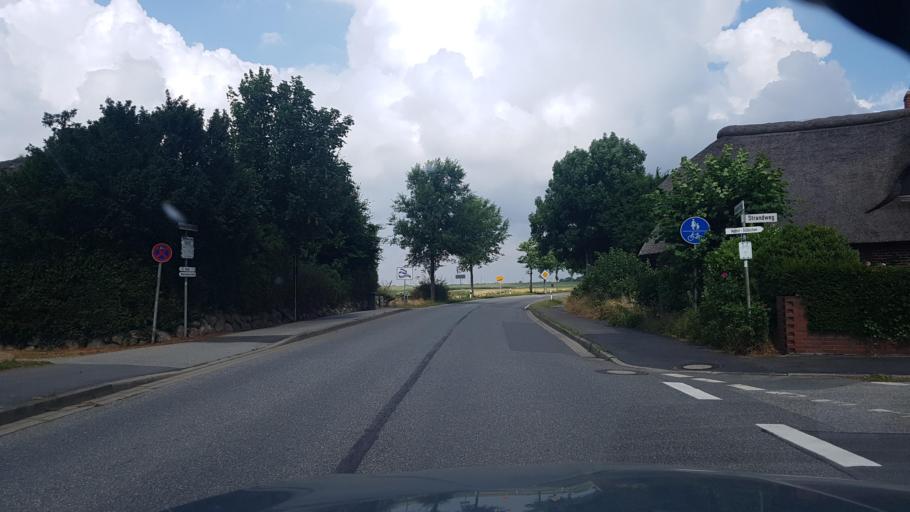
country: DE
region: Schleswig-Holstein
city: Schobull
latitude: 54.5151
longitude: 8.9955
